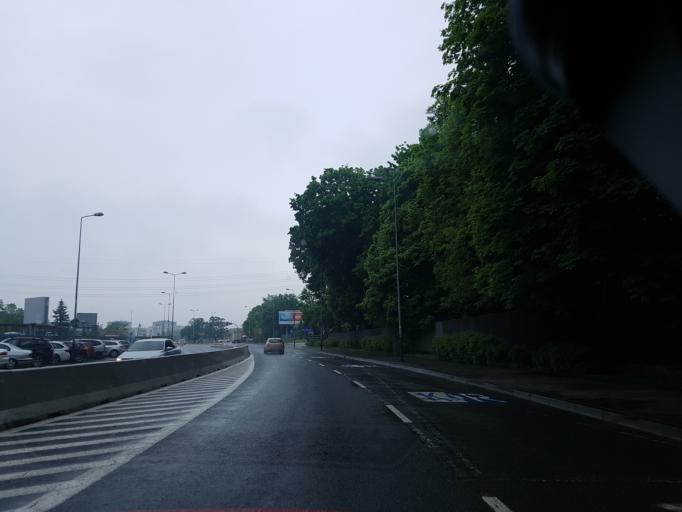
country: PL
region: Lesser Poland Voivodeship
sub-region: Krakow
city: Krakow
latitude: 50.0531
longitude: 19.9536
